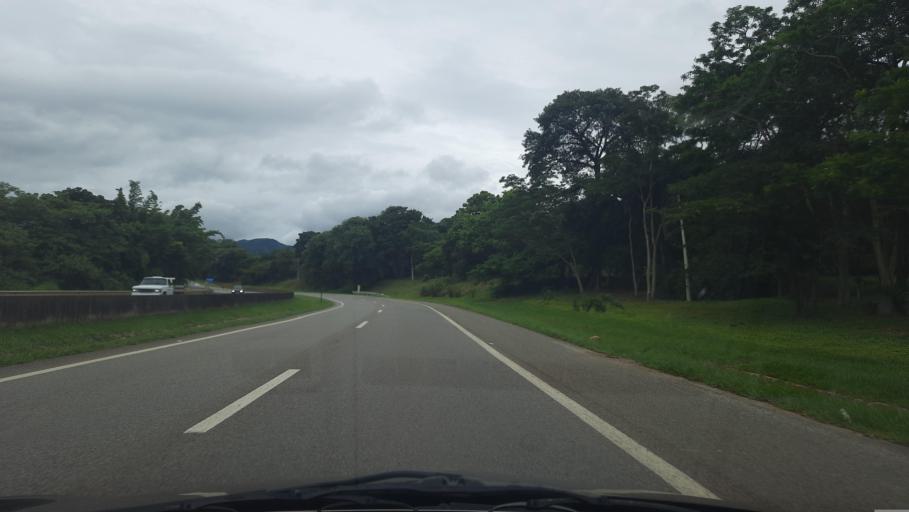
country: BR
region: Sao Paulo
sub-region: Sao Joao Da Boa Vista
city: Sao Joao da Boa Vista
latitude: -21.9593
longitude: -46.7335
